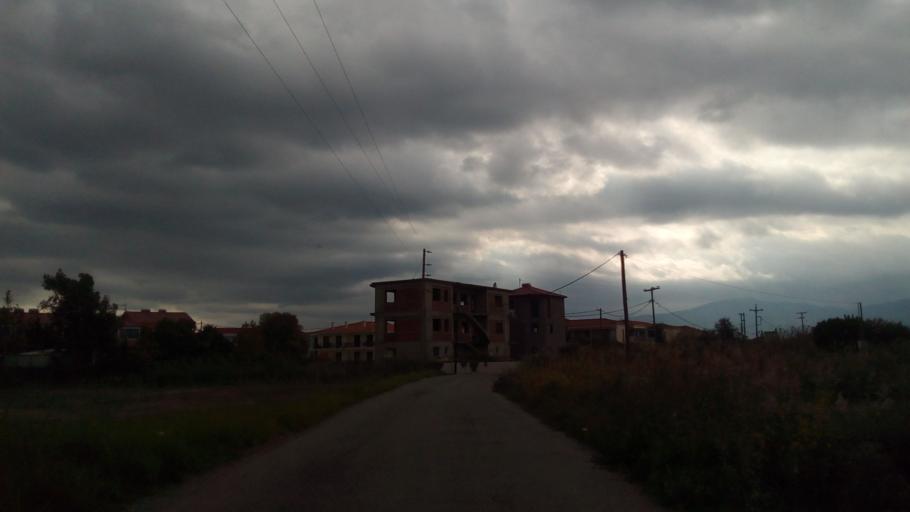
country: GR
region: West Greece
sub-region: Nomos Aitolias kai Akarnanias
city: Nafpaktos
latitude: 38.3927
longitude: 21.9171
